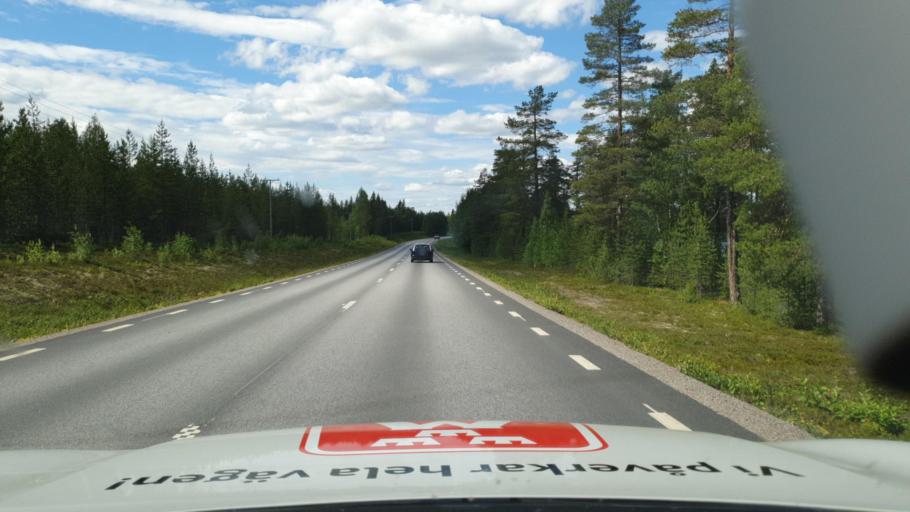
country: SE
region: Vaesterbotten
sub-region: Skelleftea Kommun
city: Langsele
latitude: 65.0205
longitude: 20.1350
